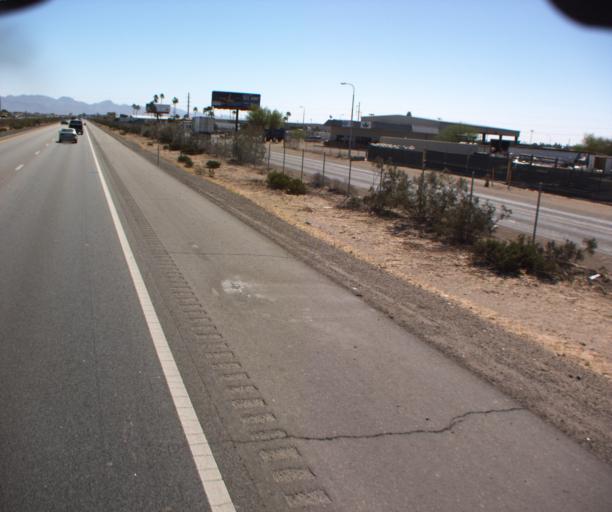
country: US
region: Arizona
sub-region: Yuma County
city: Yuma
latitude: 32.6826
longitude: -114.5585
